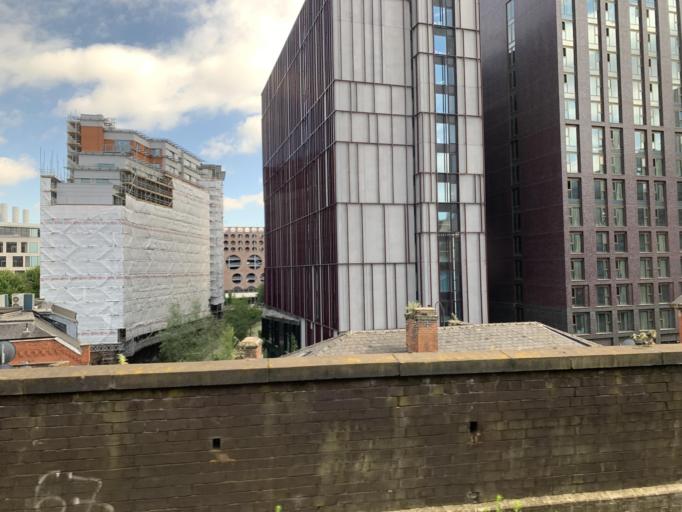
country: GB
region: England
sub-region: Manchester
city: Manchester
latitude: 53.4743
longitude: -2.2380
